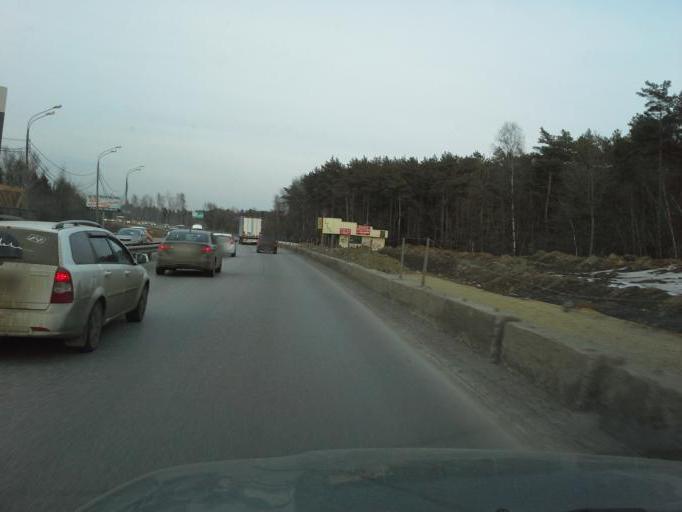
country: RU
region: Moskovskaya
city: Odintsovo
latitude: 55.6572
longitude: 37.2967
